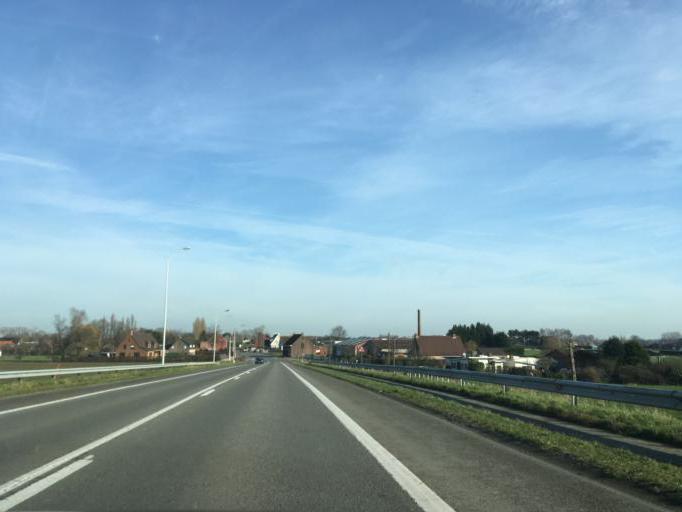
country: BE
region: Flanders
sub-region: Provincie West-Vlaanderen
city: Ardooie
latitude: 50.9643
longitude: 3.1780
